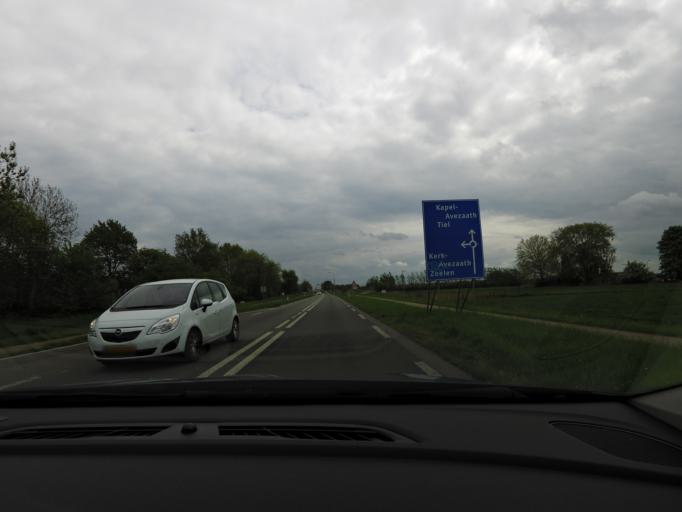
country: NL
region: Gelderland
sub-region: Gemeente Tiel
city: Tiel
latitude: 51.8964
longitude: 5.3761
